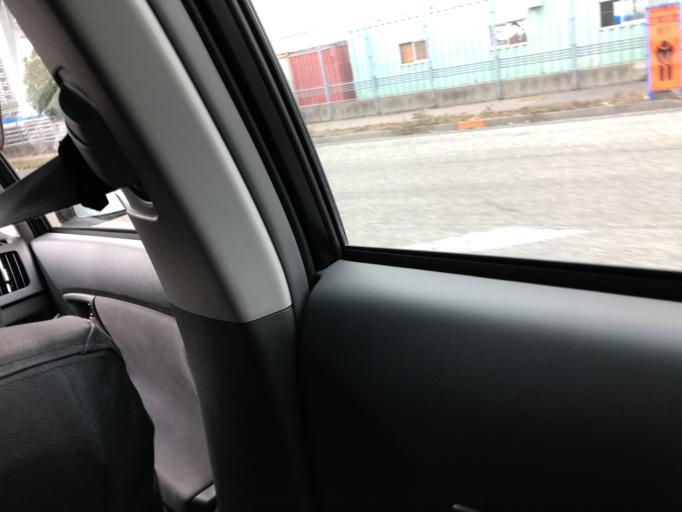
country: JP
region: Hyogo
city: Ashiya
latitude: 34.6976
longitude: 135.2738
